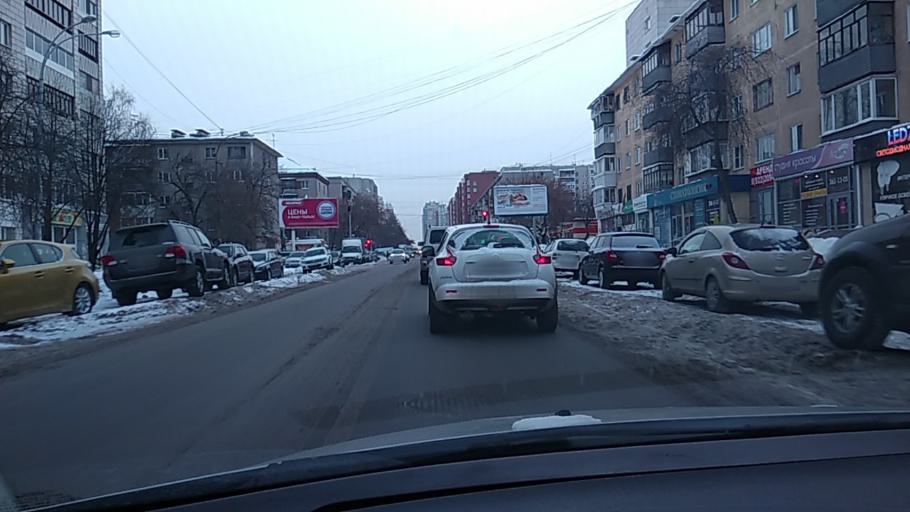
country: RU
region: Sverdlovsk
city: Yekaterinburg
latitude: 56.8136
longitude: 60.5995
